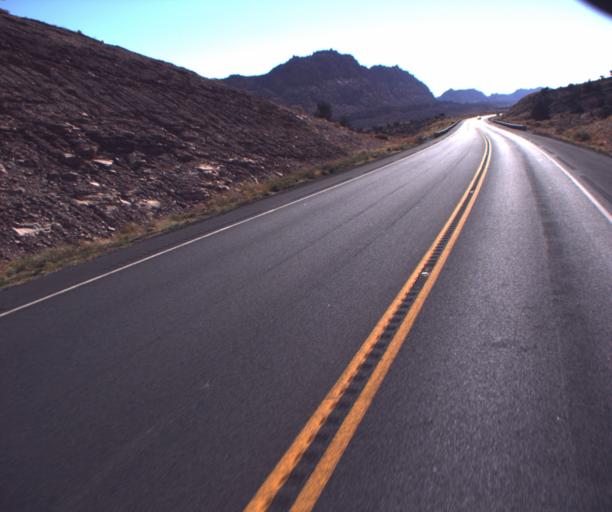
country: US
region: Arizona
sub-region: Coconino County
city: Tuba City
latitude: 36.3455
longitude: -111.5026
